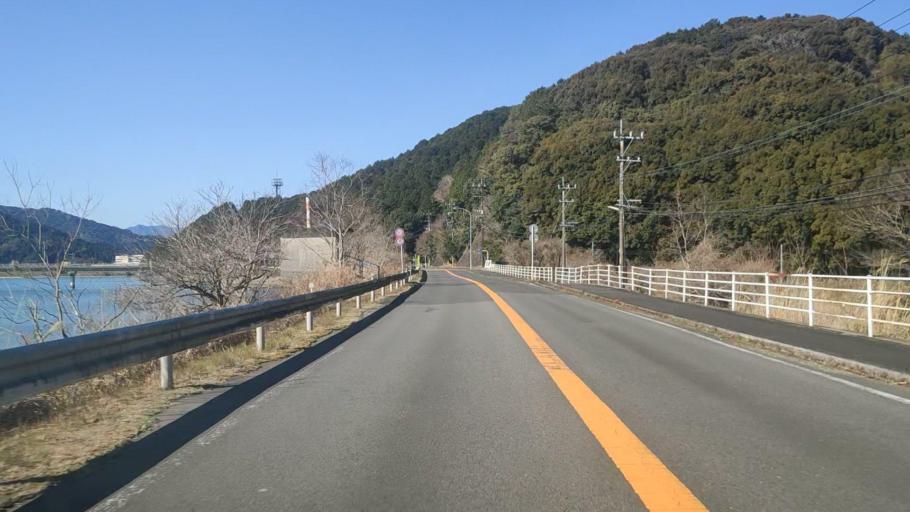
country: JP
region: Oita
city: Saiki
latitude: 32.9403
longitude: 131.9135
